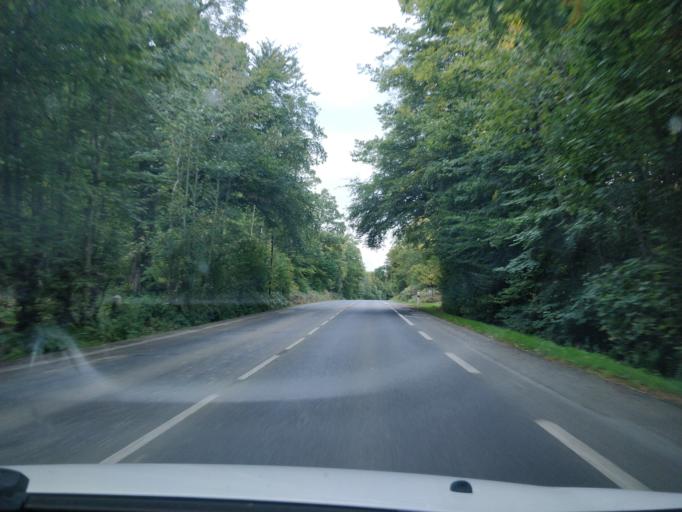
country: FR
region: Lower Normandy
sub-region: Departement du Calvados
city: Saint-Sever-Calvados
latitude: 48.8357
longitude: -1.0614
